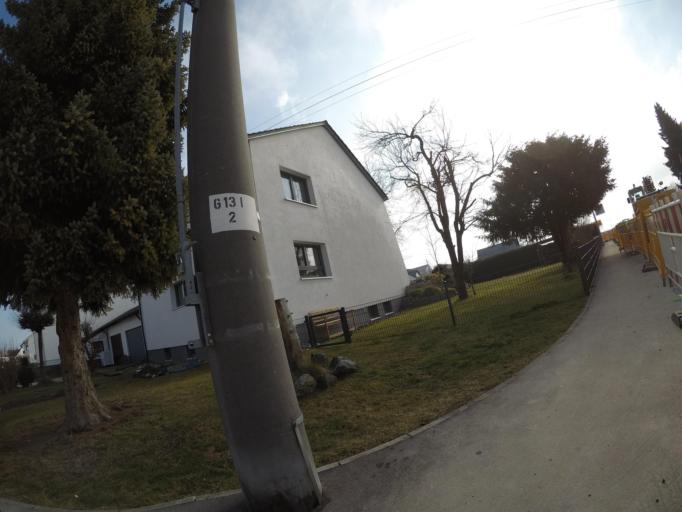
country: DE
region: Bavaria
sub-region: Swabia
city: Holzheim
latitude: 48.3781
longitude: 10.1021
